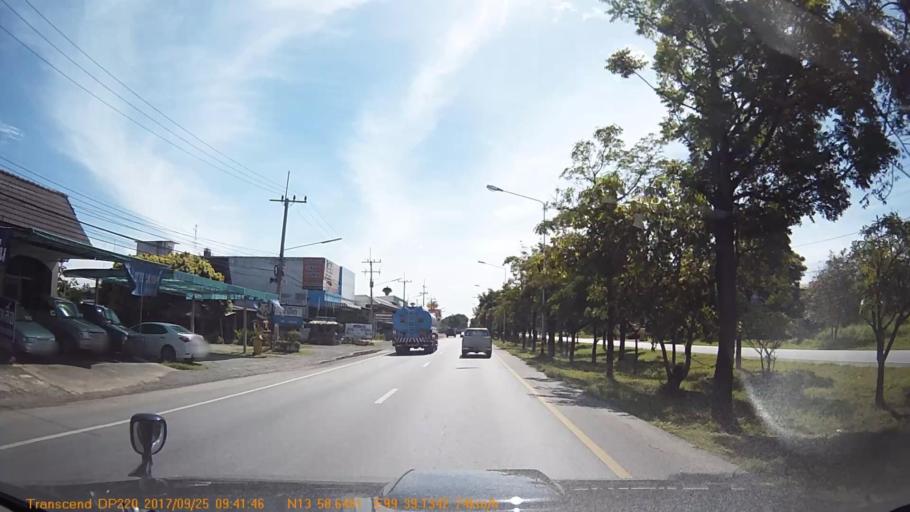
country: TH
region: Kanchanaburi
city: Tha Muang
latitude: 13.9774
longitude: 99.6526
